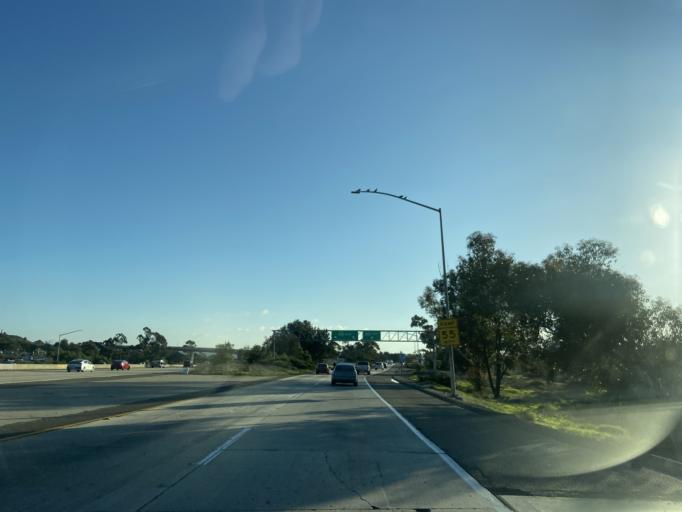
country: US
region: California
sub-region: San Diego County
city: Imperial Beach
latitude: 32.5735
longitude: -117.0397
